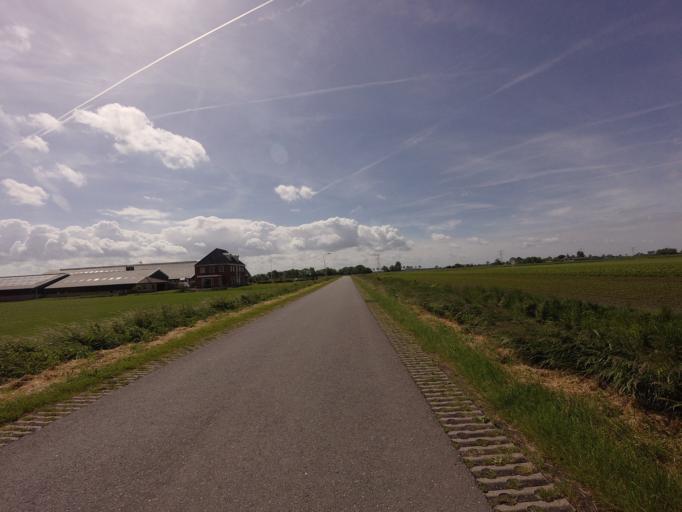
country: NL
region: North Holland
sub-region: Gemeente Opmeer
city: Opmeer
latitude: 52.6568
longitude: 4.9865
